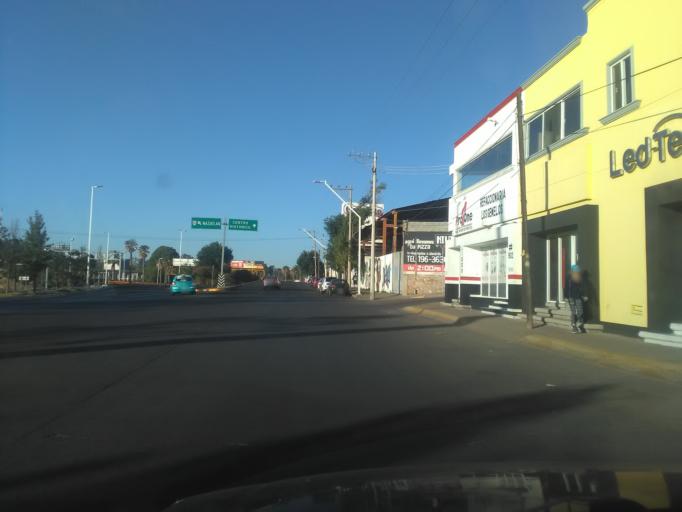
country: MX
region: Durango
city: Victoria de Durango
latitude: 24.0332
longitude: -104.6851
